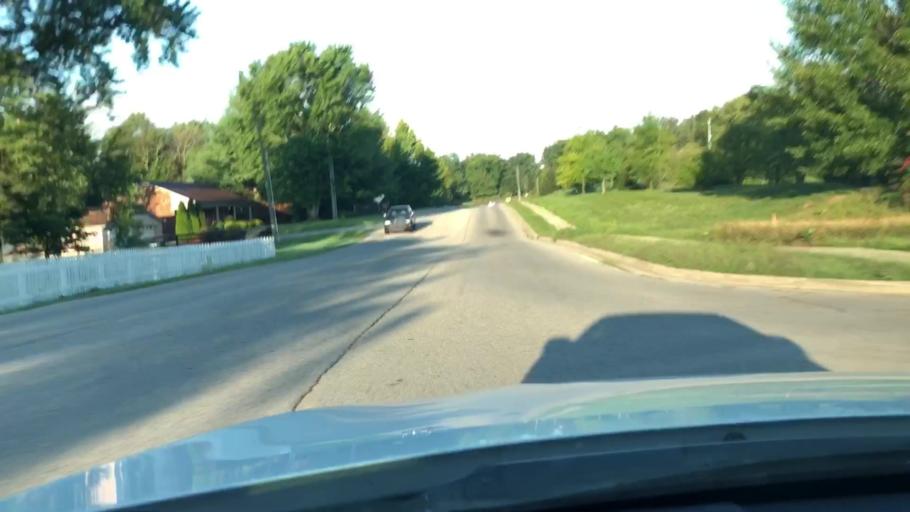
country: US
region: Kentucky
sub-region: Jefferson County
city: Middletown
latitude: 38.2172
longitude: -85.5286
